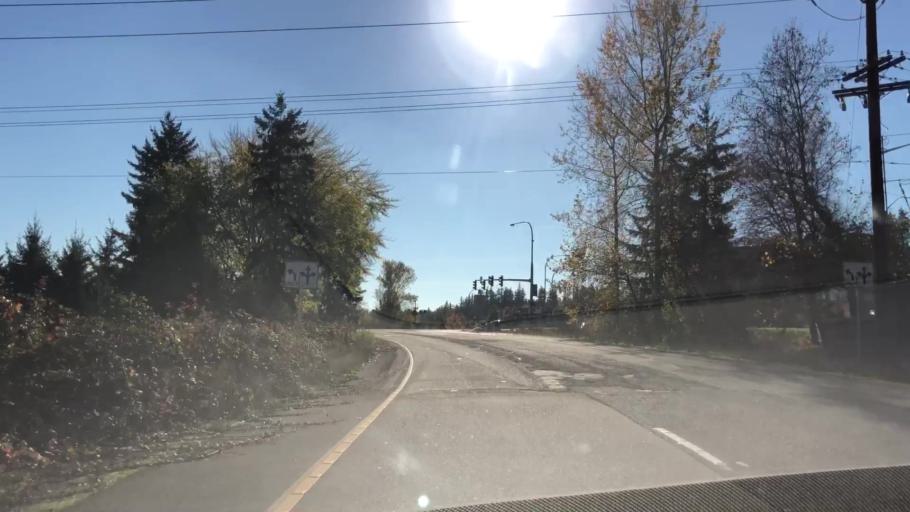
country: US
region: Washington
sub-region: King County
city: Bothell
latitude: 47.7693
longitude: -122.1906
